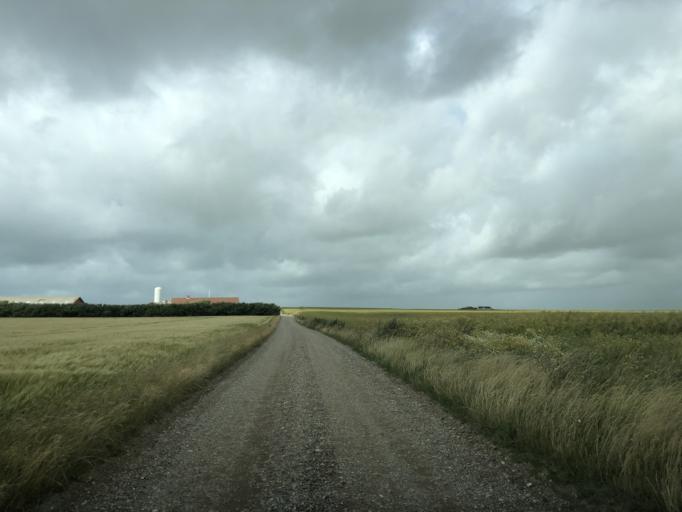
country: DK
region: Central Jutland
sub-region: Lemvig Kommune
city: Harboore
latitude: 56.4998
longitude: 8.1283
